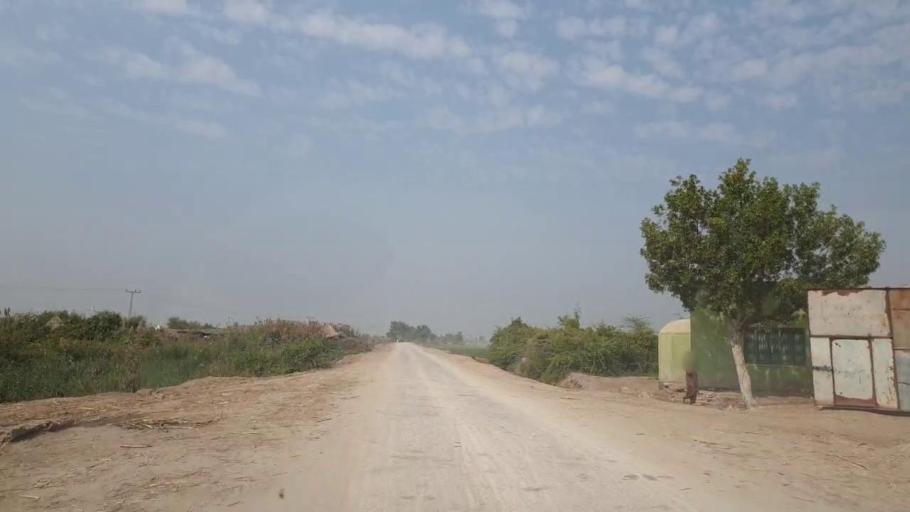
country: PK
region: Sindh
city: Mirpur Khas
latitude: 25.5462
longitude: 69.0819
